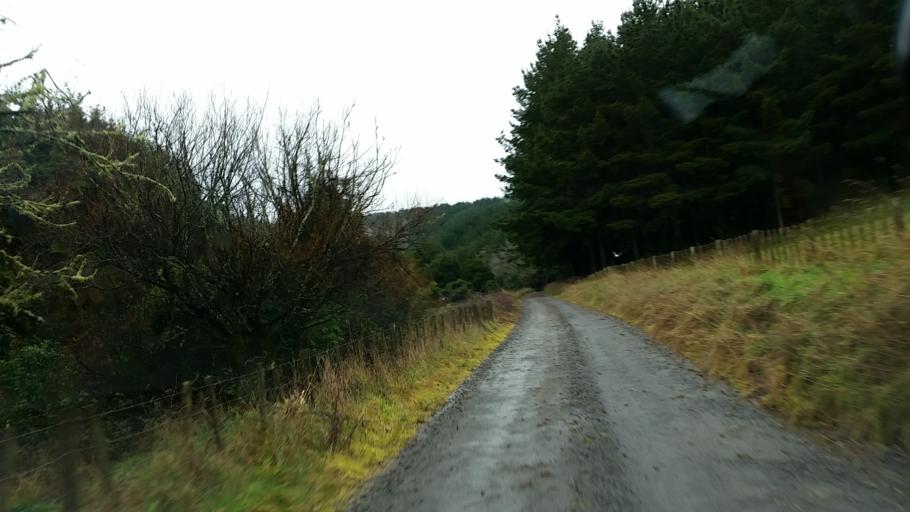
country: NZ
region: Taranaki
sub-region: South Taranaki District
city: Eltham
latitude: -39.5019
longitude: 174.4252
